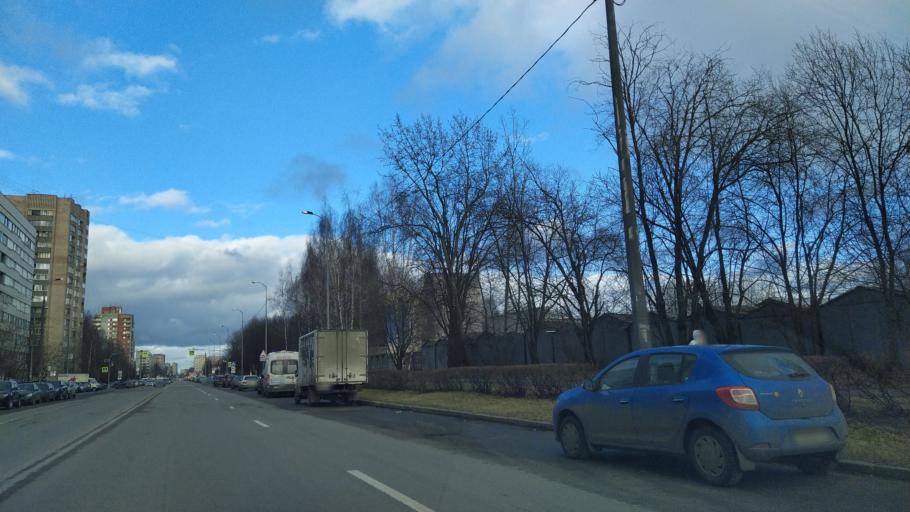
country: RU
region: St.-Petersburg
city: Grazhdanka
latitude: 60.0371
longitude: 30.3822
